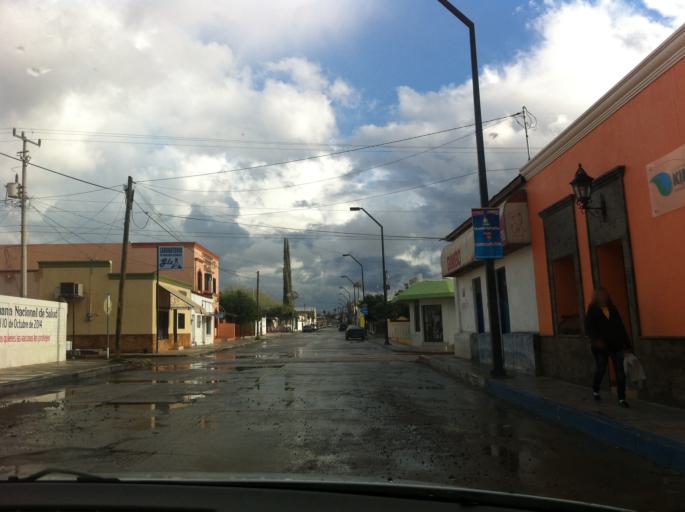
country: MX
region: Sonora
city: Magdalena de Kino
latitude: 30.6294
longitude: -110.9722
